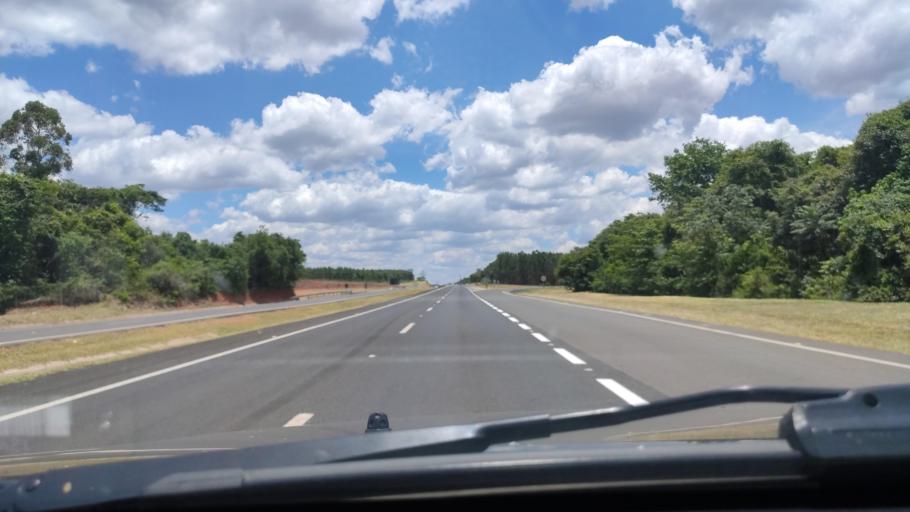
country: BR
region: Sao Paulo
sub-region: Duartina
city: Duartina
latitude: -22.5105
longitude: -49.3004
